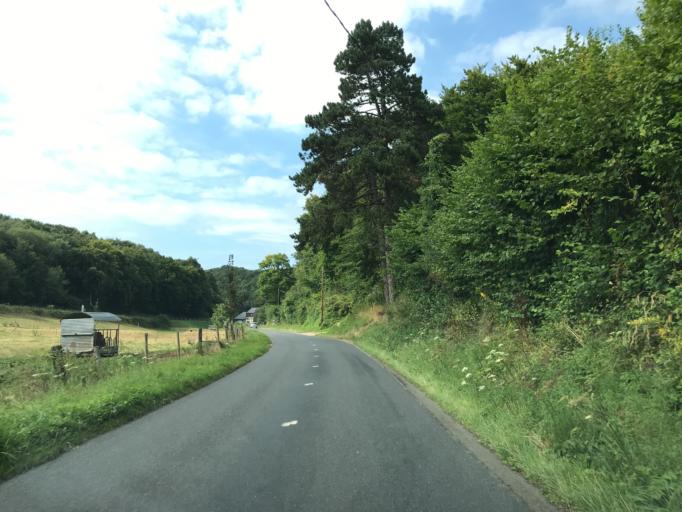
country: FR
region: Haute-Normandie
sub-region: Departement de la Seine-Maritime
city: Yport
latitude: 49.7280
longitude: 0.3381
